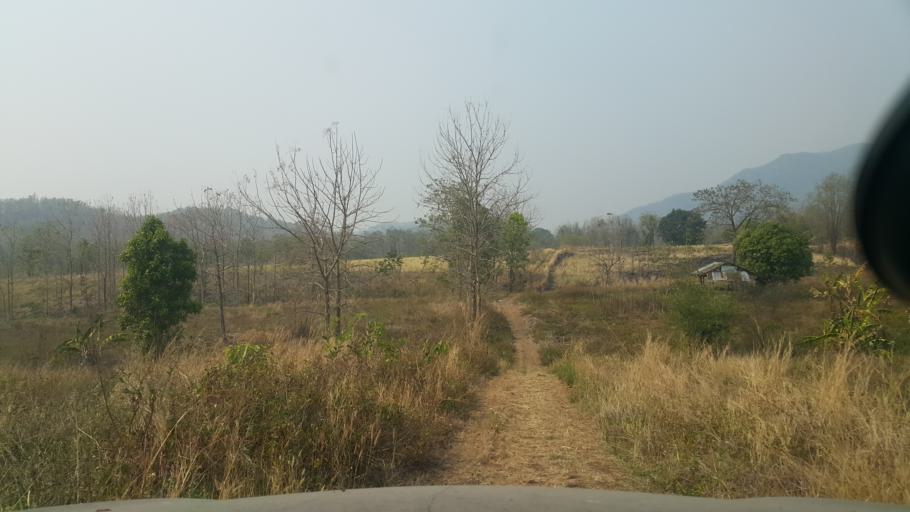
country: TH
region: Chiang Mai
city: Mae On
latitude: 18.7642
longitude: 99.2712
